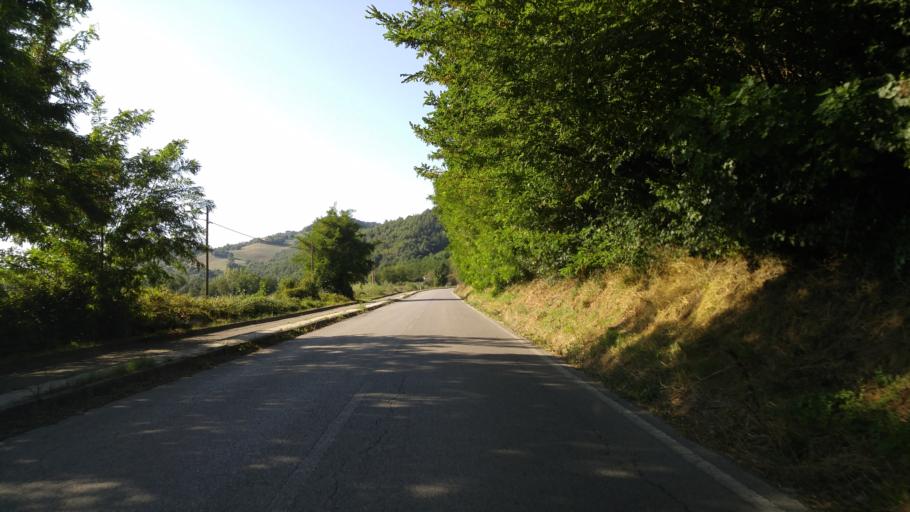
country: IT
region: The Marches
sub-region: Provincia di Pesaro e Urbino
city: Urbania
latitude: 43.6782
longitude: 12.5217
